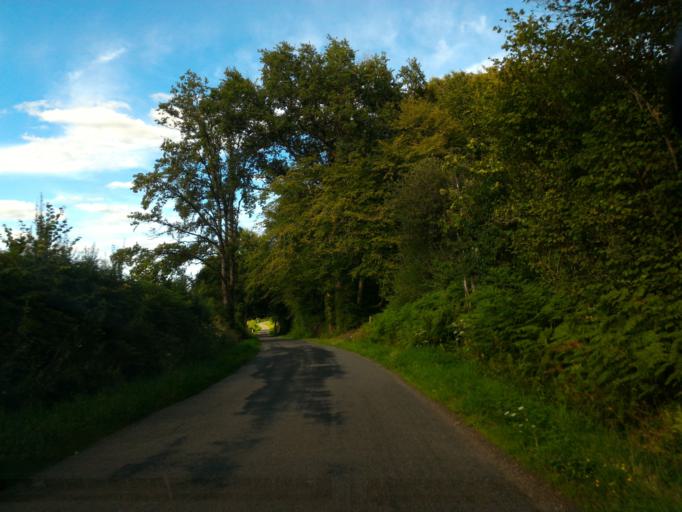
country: FR
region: Poitou-Charentes
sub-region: Departement de la Charente
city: Brigueuil
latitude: 45.9826
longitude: 0.8228
